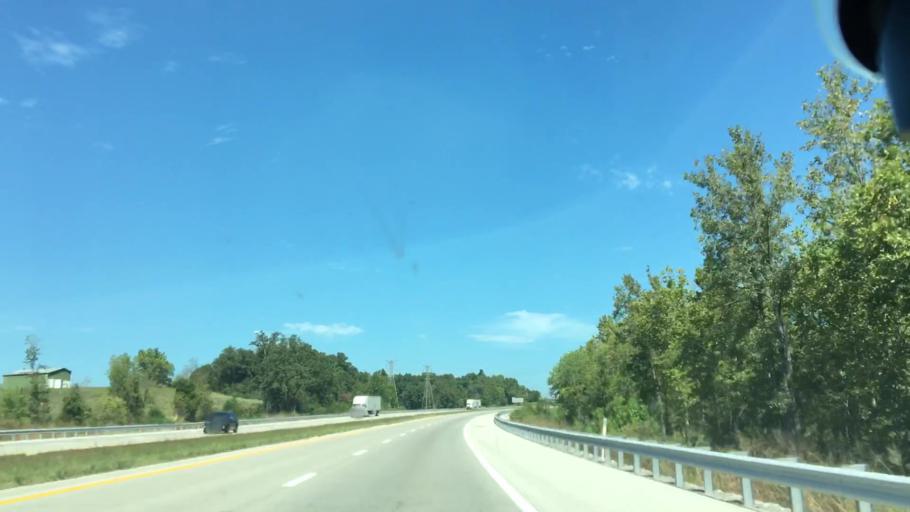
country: US
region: Kentucky
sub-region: Christian County
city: Hopkinsville
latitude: 36.9166
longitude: -87.4741
